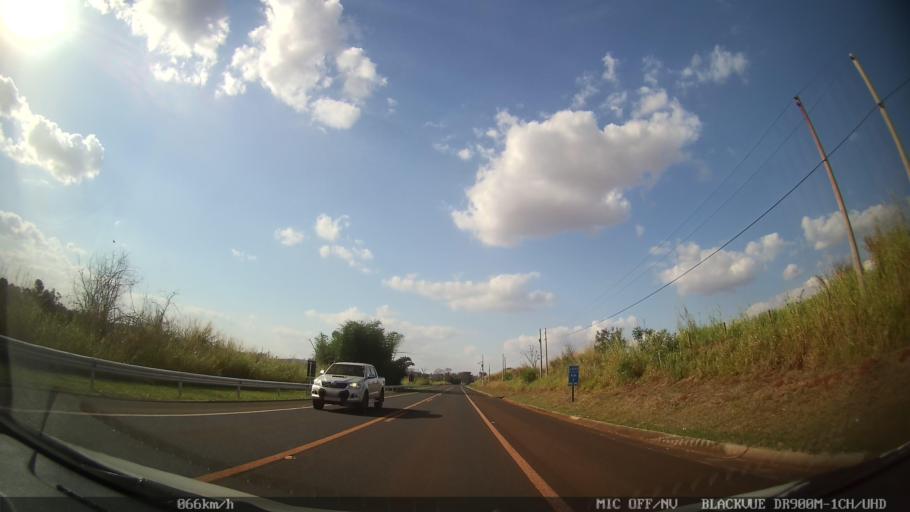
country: BR
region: Sao Paulo
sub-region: Ribeirao Preto
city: Ribeirao Preto
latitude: -21.1870
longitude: -47.8633
